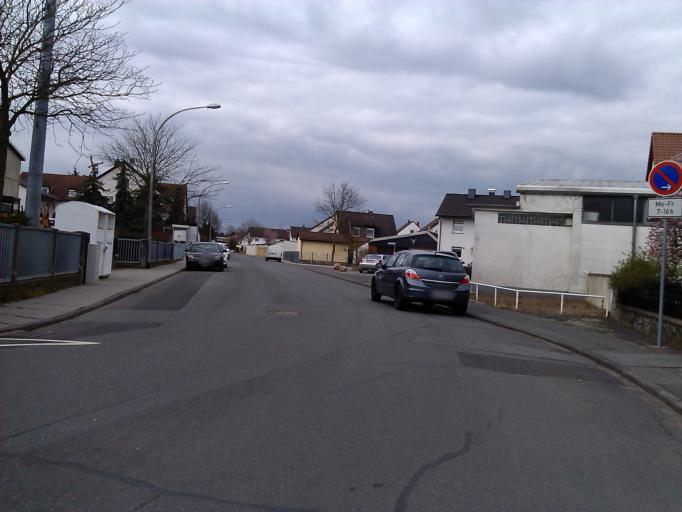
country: DE
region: Hesse
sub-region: Regierungsbezirk Darmstadt
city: Nauheim
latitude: 49.9442
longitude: 8.4476
